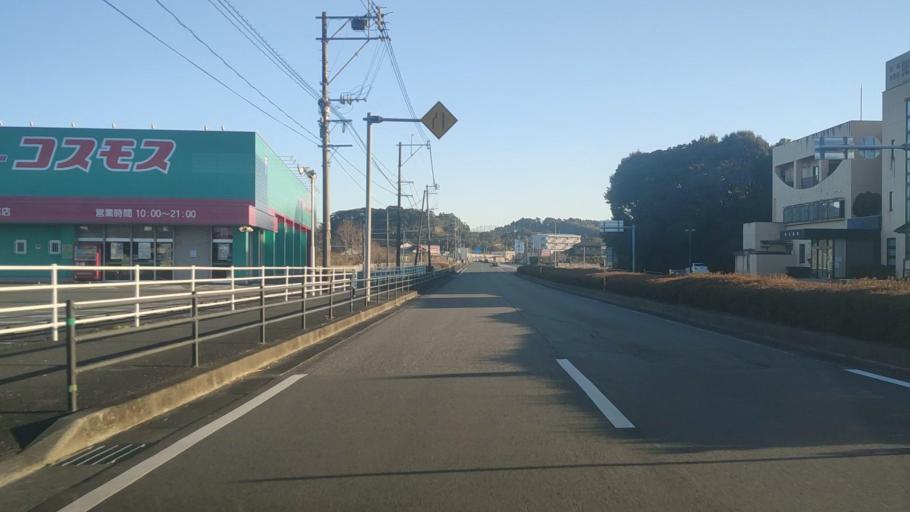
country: JP
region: Miyazaki
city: Takanabe
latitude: 32.0710
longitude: 131.4915
